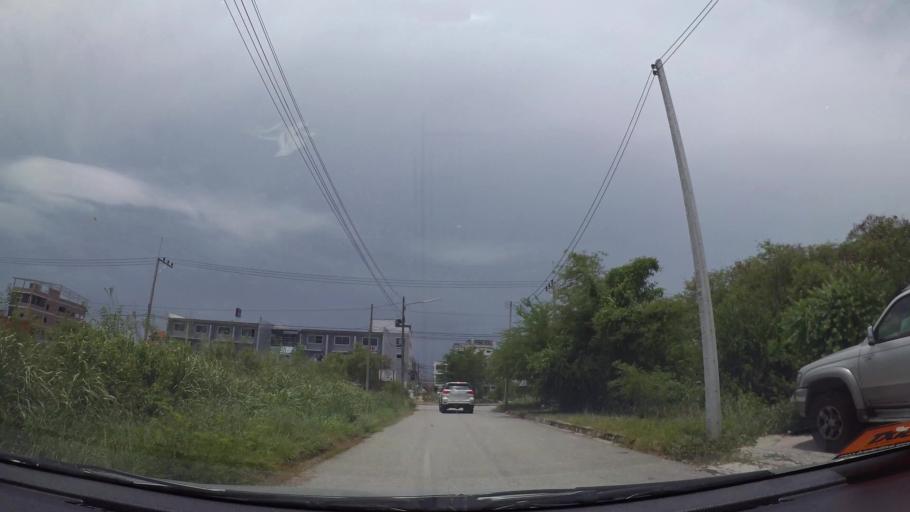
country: TH
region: Chon Buri
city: Chon Buri
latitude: 13.3391
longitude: 100.9515
